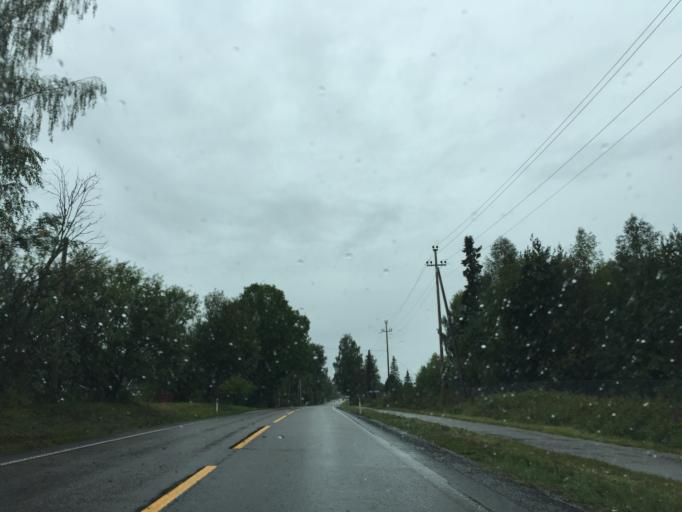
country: NO
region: Akershus
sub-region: Nes
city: Neskollen
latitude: 60.1427
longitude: 11.3968
